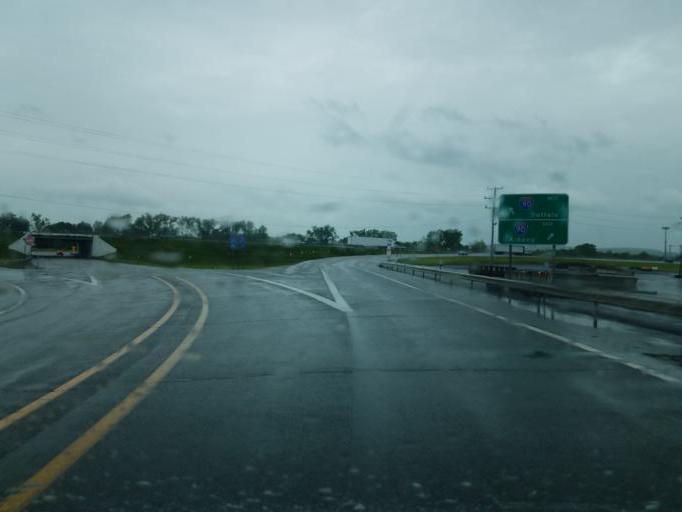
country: US
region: New York
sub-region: Herkimer County
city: Herkimer
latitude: 43.0163
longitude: -74.9897
